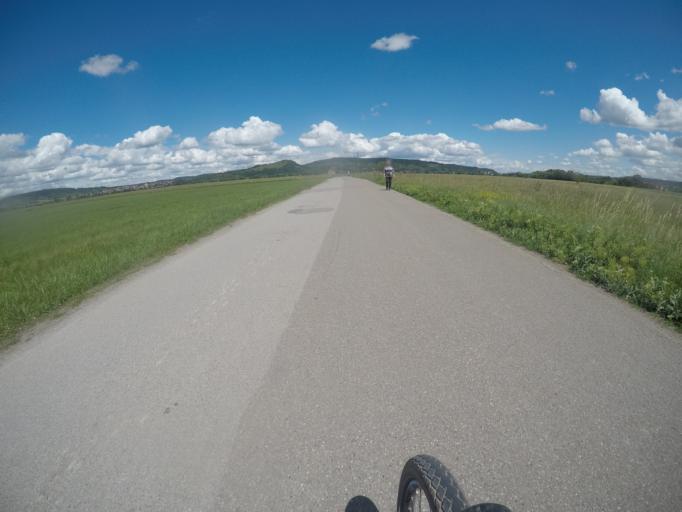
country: DE
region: Baden-Wuerttemberg
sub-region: Tuebingen Region
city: Rottenburg
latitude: 48.4849
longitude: 8.9680
